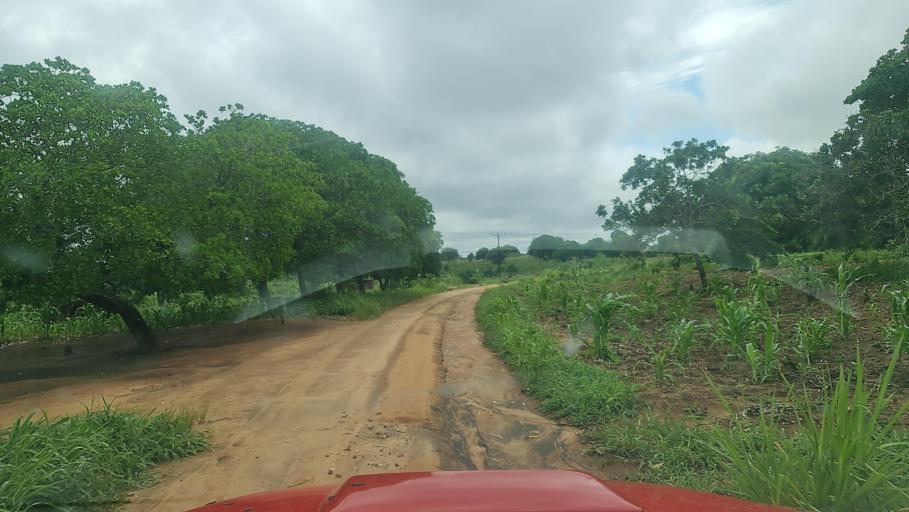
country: MW
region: Southern Region
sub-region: Nsanje District
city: Nsanje
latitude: -17.1808
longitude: 35.9113
